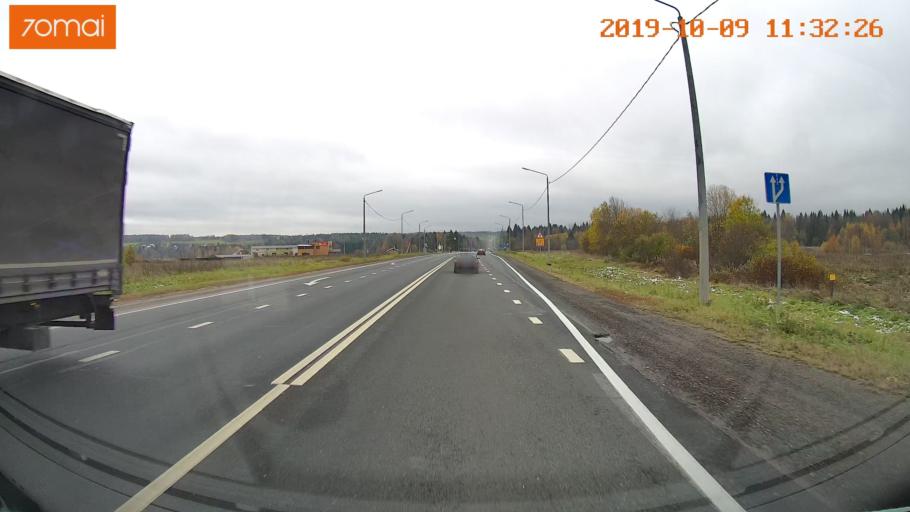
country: RU
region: Vologda
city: Gryazovets
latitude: 59.0357
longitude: 40.1081
